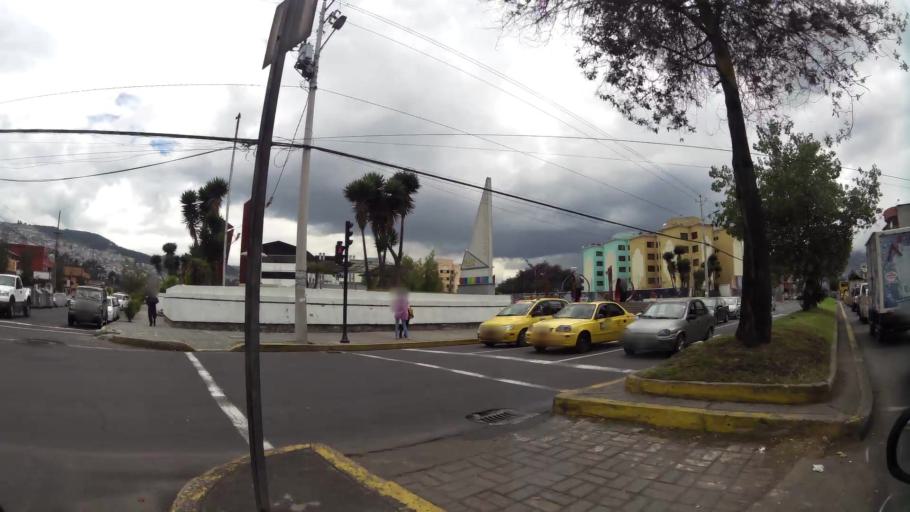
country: EC
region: Pichincha
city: Quito
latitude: -0.2475
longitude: -78.5250
